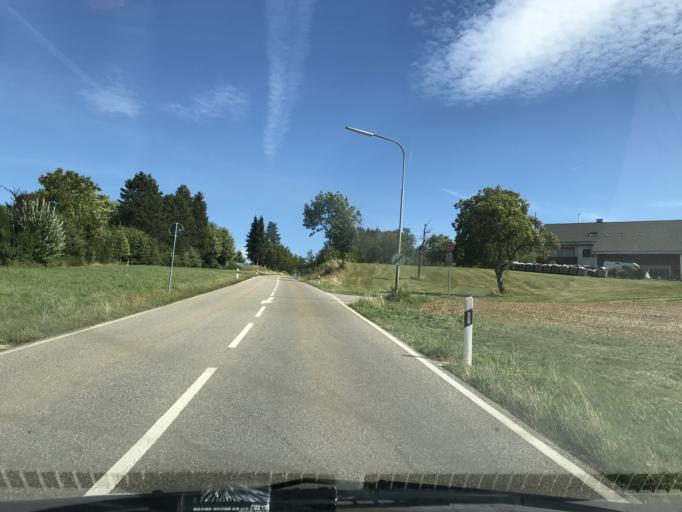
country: DE
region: Baden-Wuerttemberg
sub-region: Freiburg Region
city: Schopfheim
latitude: 47.6429
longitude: 7.8323
